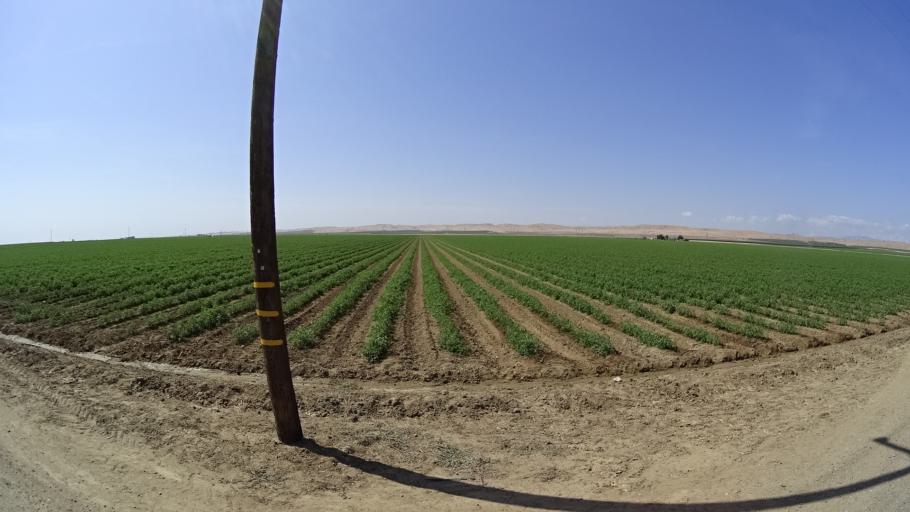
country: US
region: California
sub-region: Kings County
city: Kettleman City
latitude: 36.0725
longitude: -120.0336
